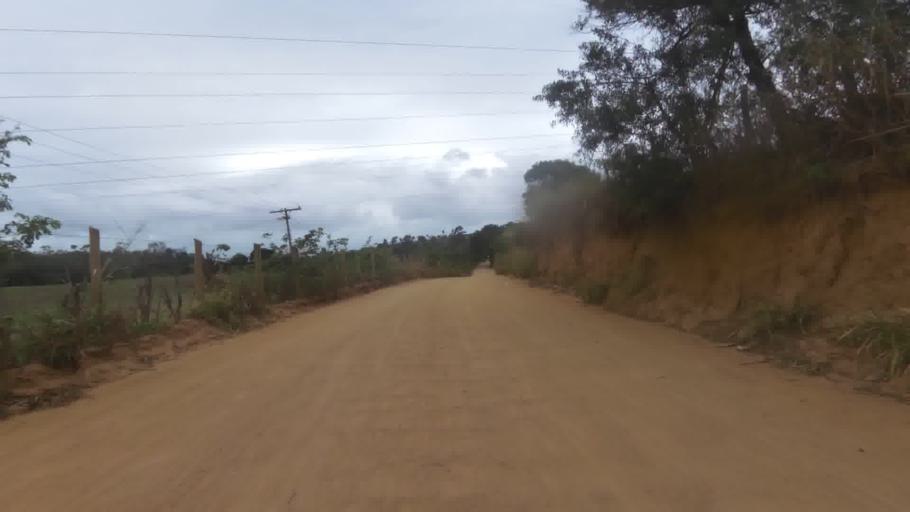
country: BR
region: Espirito Santo
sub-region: Viana
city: Viana
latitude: -20.5224
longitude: -40.4719
